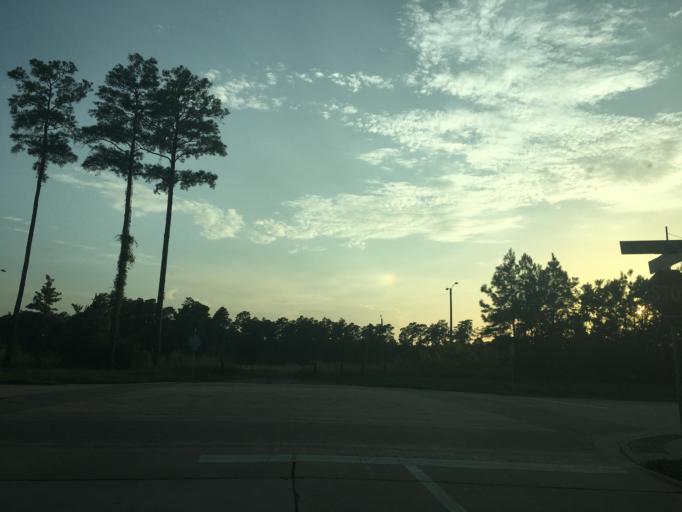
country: US
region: Texas
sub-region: Harris County
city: Spring
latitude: 30.0971
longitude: -95.4448
